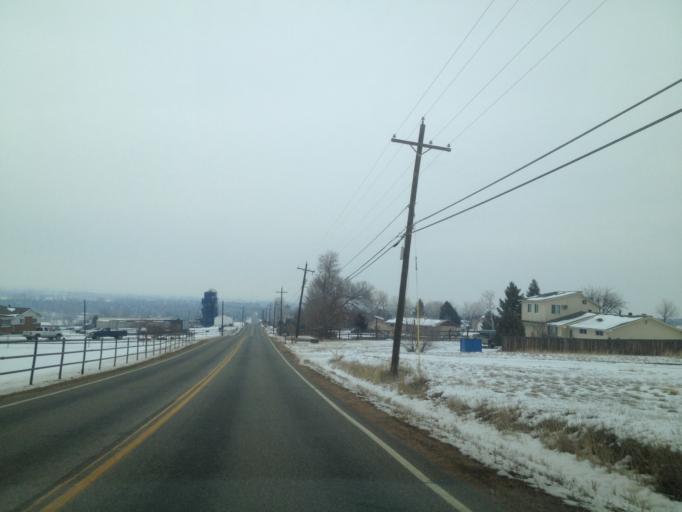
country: US
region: Colorado
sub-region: Boulder County
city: Gunbarrel
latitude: 40.0808
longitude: -105.1691
